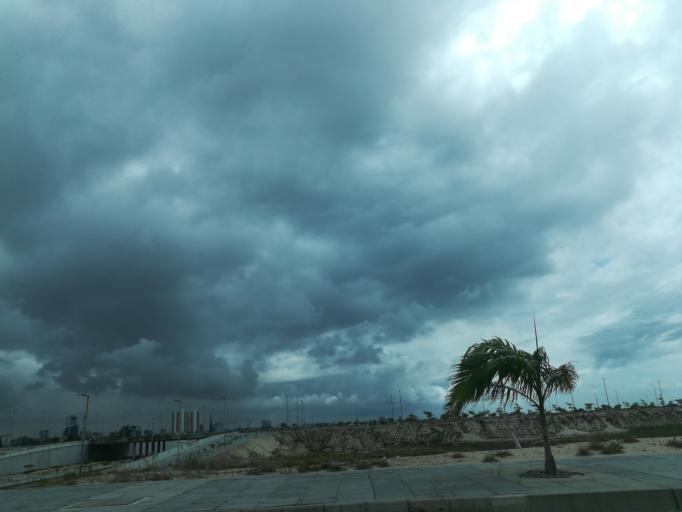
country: NG
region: Lagos
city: Ikoyi
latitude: 6.4119
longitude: 3.4146
